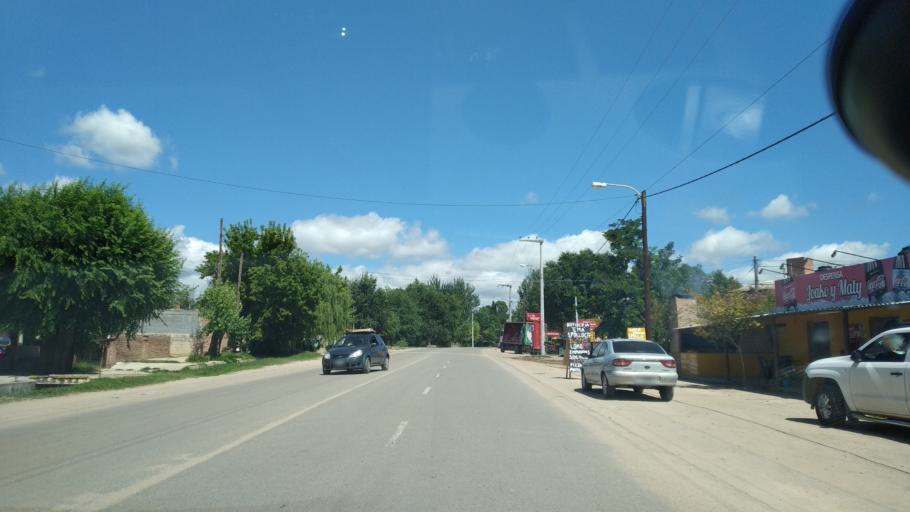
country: AR
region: Cordoba
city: Villa Cura Brochero
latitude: -31.7056
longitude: -65.0224
